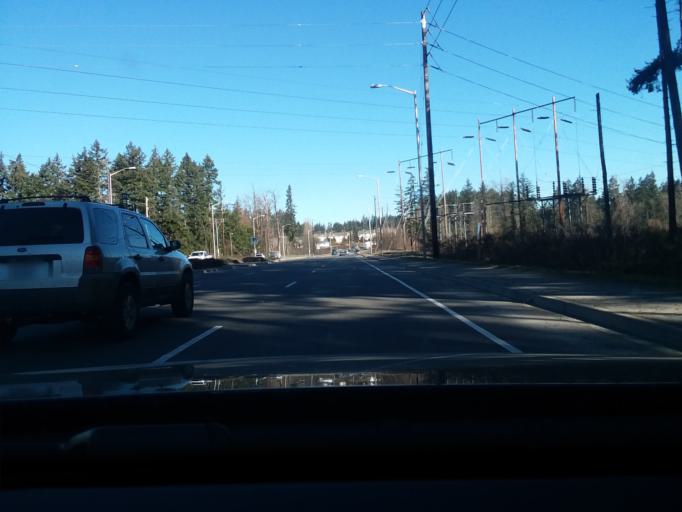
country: US
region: Washington
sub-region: Pierce County
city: Frederickson
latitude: 47.1005
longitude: -122.3569
